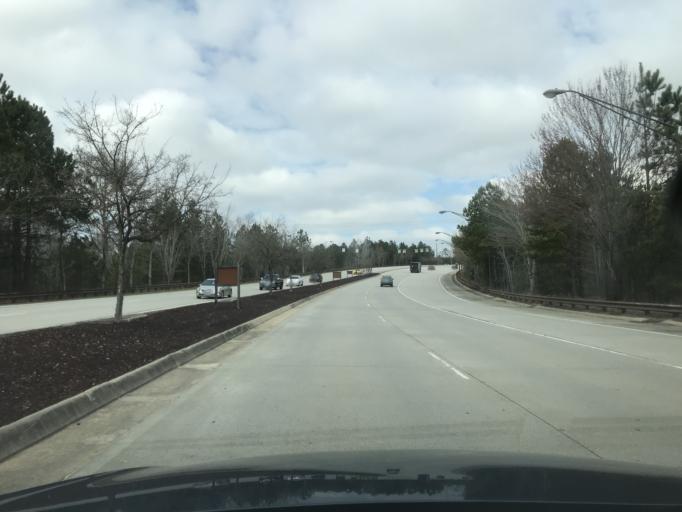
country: US
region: Georgia
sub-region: Columbia County
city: Grovetown
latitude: 33.4372
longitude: -82.1182
